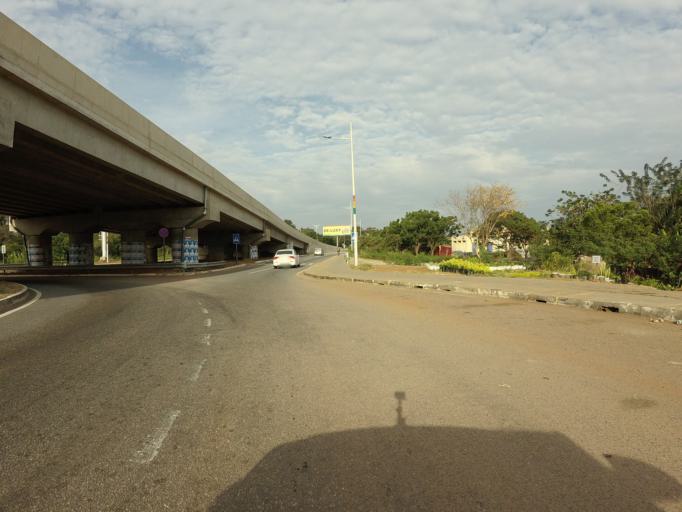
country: GH
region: Greater Accra
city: Accra
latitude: 5.5878
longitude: -0.1651
